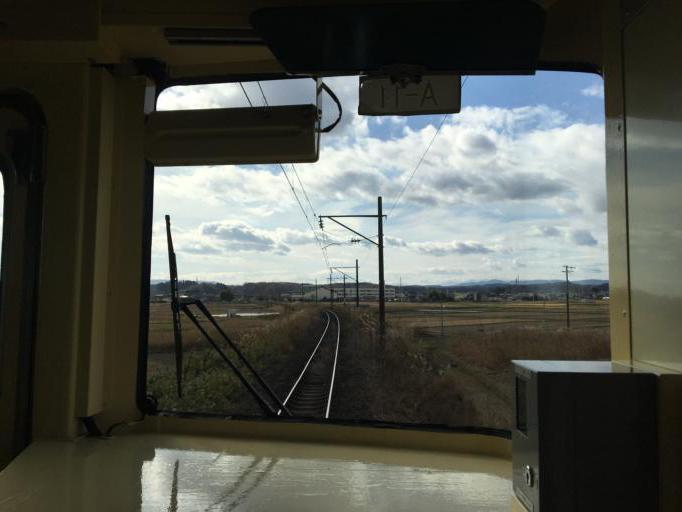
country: JP
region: Miyagi
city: Watari
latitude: 38.0581
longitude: 140.7952
